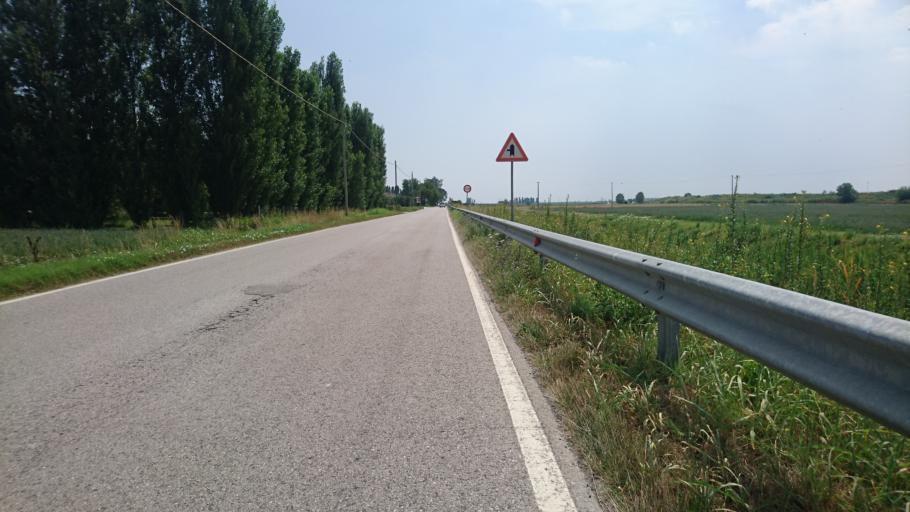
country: IT
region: Veneto
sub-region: Provincia di Rovigo
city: Rosolina
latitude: 45.0664
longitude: 12.2583
